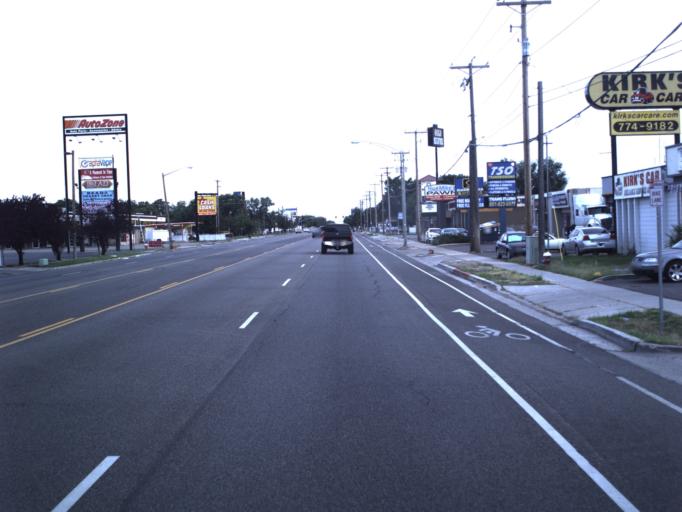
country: US
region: Utah
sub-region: Weber County
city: Roy
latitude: 41.1586
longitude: -112.0261
